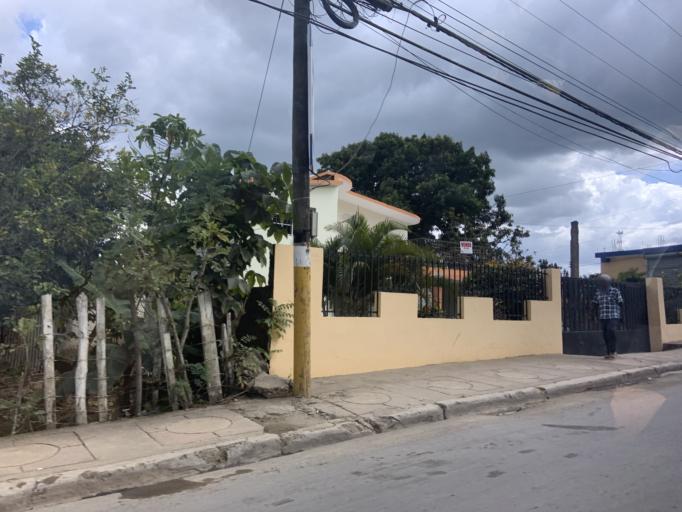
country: DO
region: Monte Plata
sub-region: Yamasa
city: Yamasa
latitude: 18.7785
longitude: -70.0256
